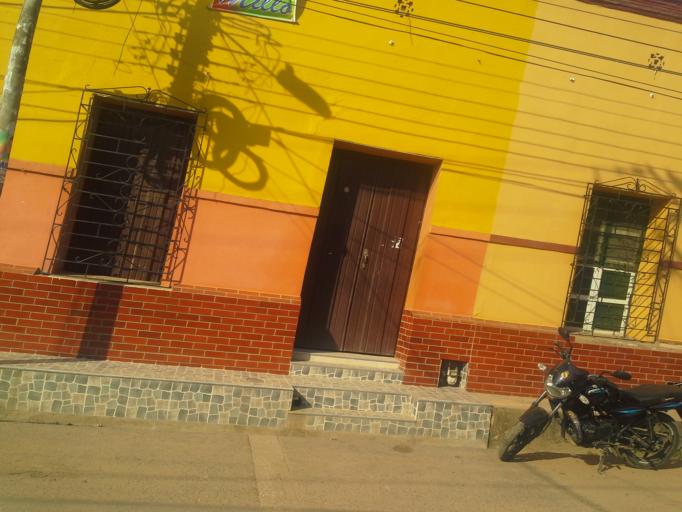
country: CO
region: Bolivar
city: El Carmen de Bolivar
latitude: 9.7146
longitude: -75.1181
